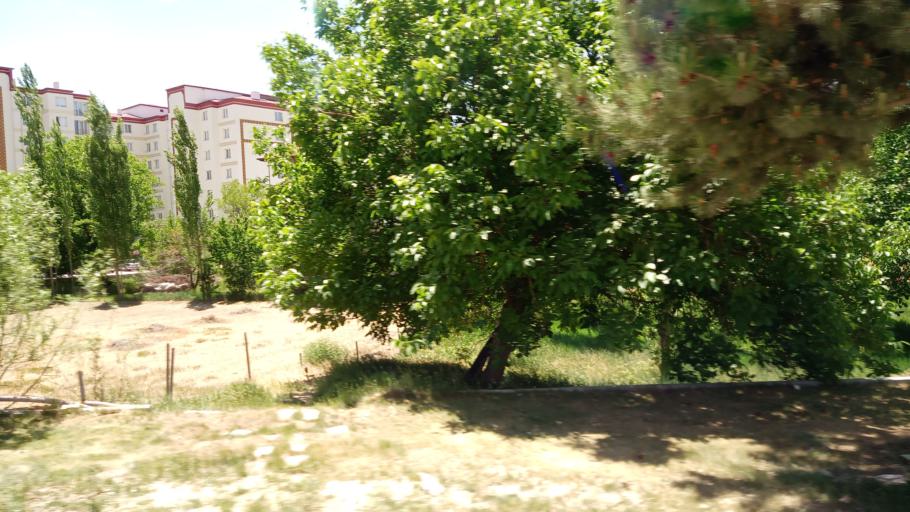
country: TR
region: Sivas
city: Gurun
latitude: 38.7212
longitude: 37.2767
